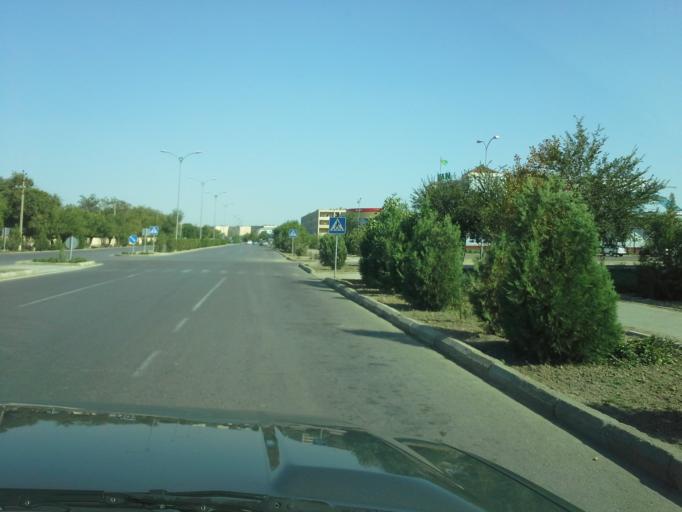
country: TM
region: Dasoguz
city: Dasoguz
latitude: 41.8234
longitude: 59.9666
